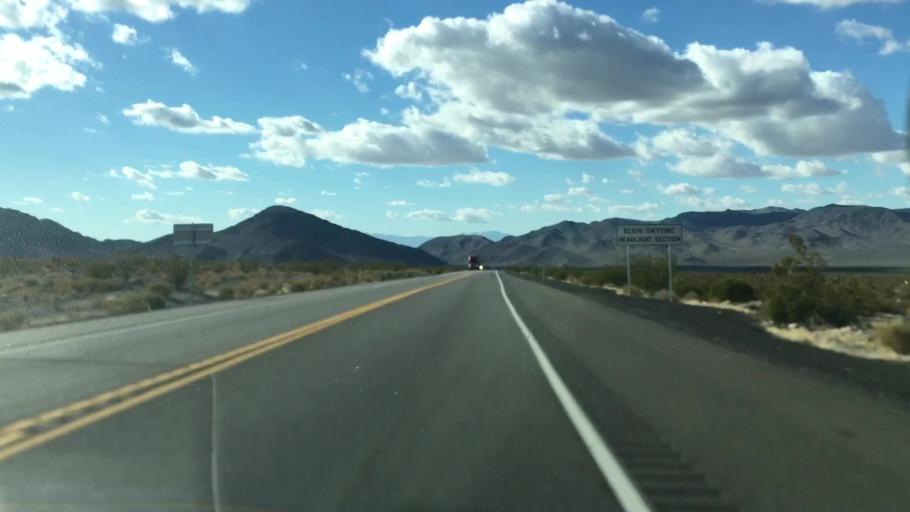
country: US
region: Nevada
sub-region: Nye County
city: Pahrump
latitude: 36.5951
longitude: -116.0132
